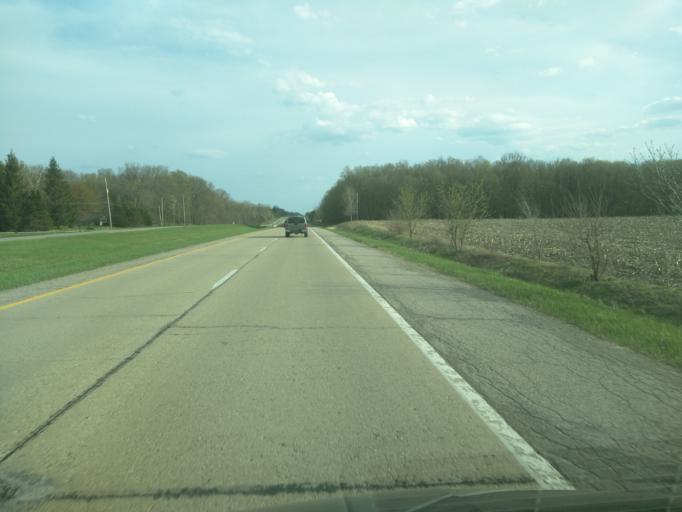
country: US
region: Michigan
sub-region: Eaton County
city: Dimondale
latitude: 42.6356
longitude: -84.6232
